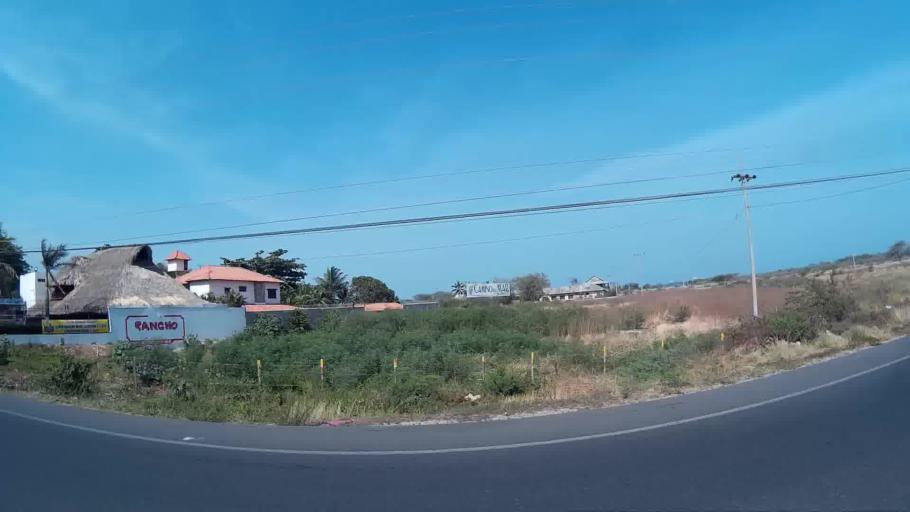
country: CO
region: Magdalena
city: Santa Marta
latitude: 11.1608
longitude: -74.2245
